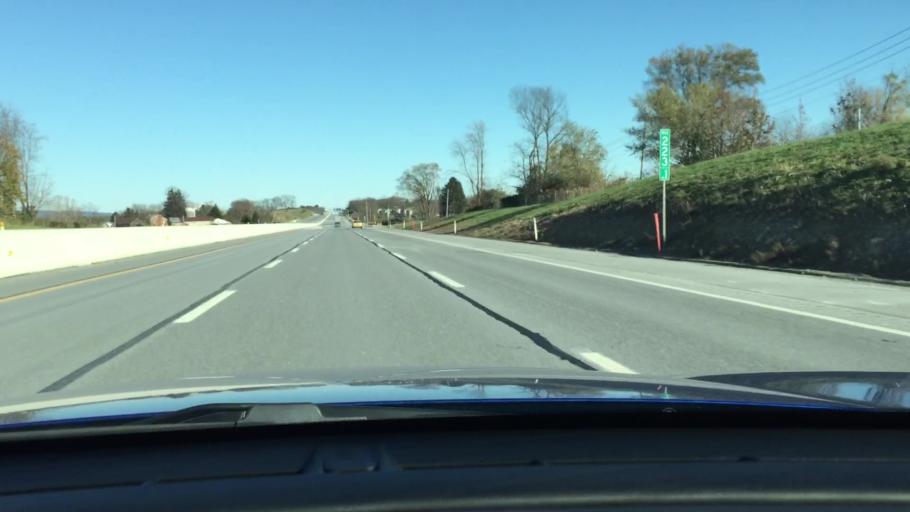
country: US
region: Pennsylvania
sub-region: Cumberland County
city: Carlisle
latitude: 40.2137
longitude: -77.2136
